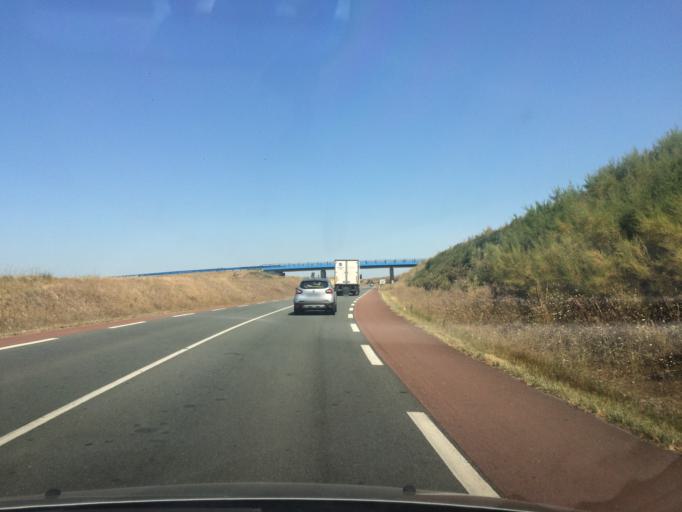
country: FR
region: Poitou-Charentes
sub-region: Departement de la Charente-Maritime
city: Esnandes
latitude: 46.2369
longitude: -1.0777
